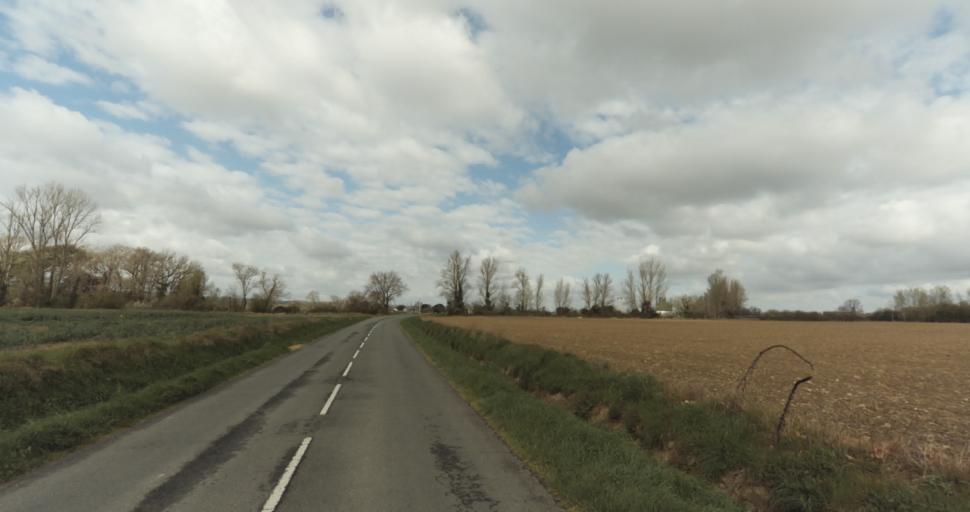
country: FR
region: Midi-Pyrenees
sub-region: Departement de la Haute-Garonne
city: Miremont
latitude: 43.3602
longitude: 1.4471
